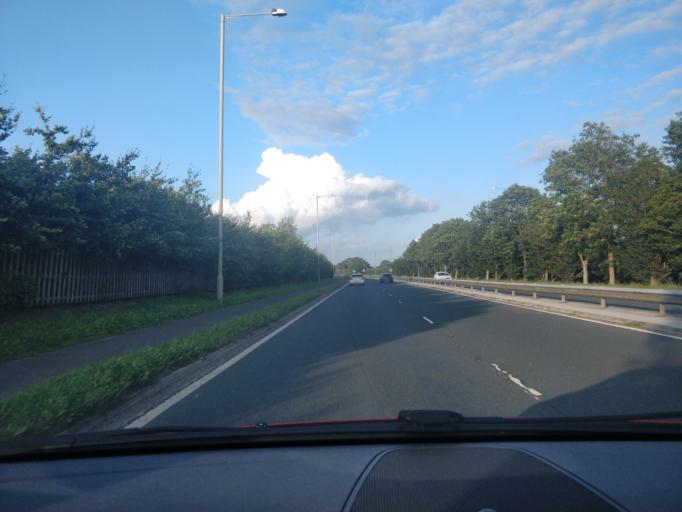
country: GB
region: England
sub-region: Lancashire
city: Tarleton
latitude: 53.7079
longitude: -2.7912
